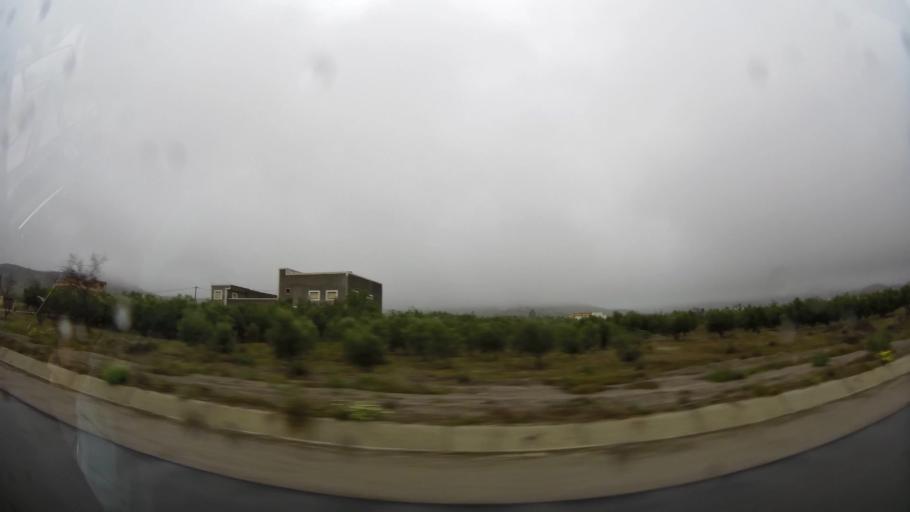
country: MA
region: Oriental
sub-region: Nador
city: Midar
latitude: 34.8386
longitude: -3.7206
